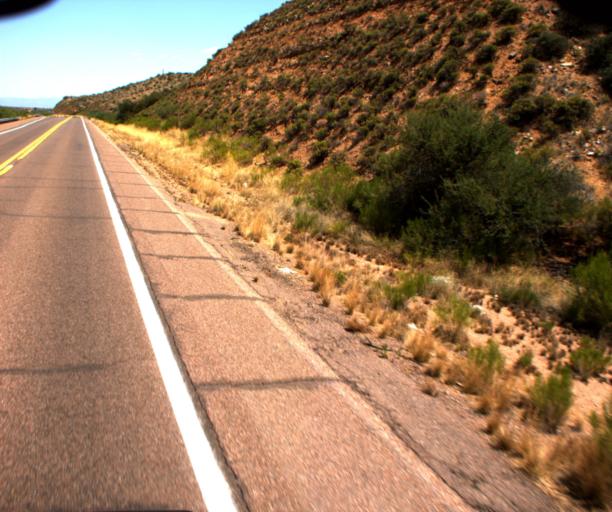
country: US
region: Arizona
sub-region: Gila County
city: Tonto Basin
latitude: 33.7452
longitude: -111.2303
